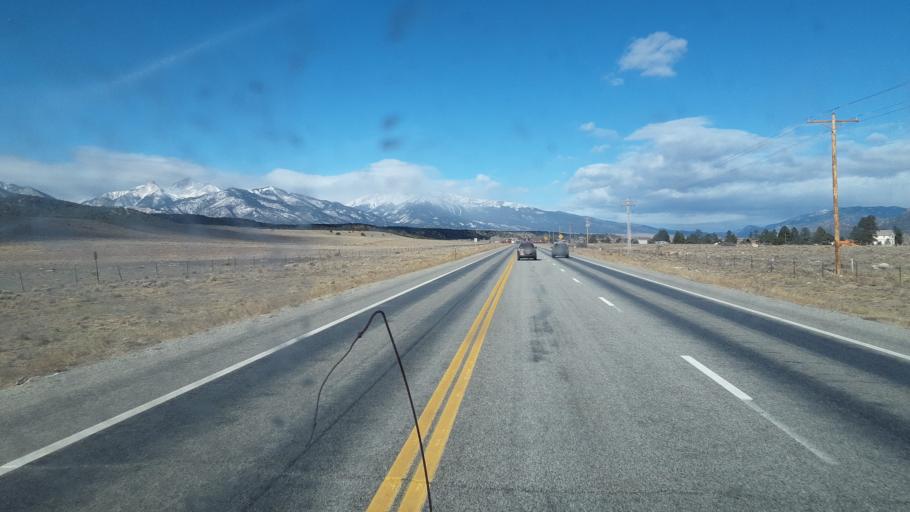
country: US
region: Colorado
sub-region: Chaffee County
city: Buena Vista
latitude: 38.7563
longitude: -106.0845
